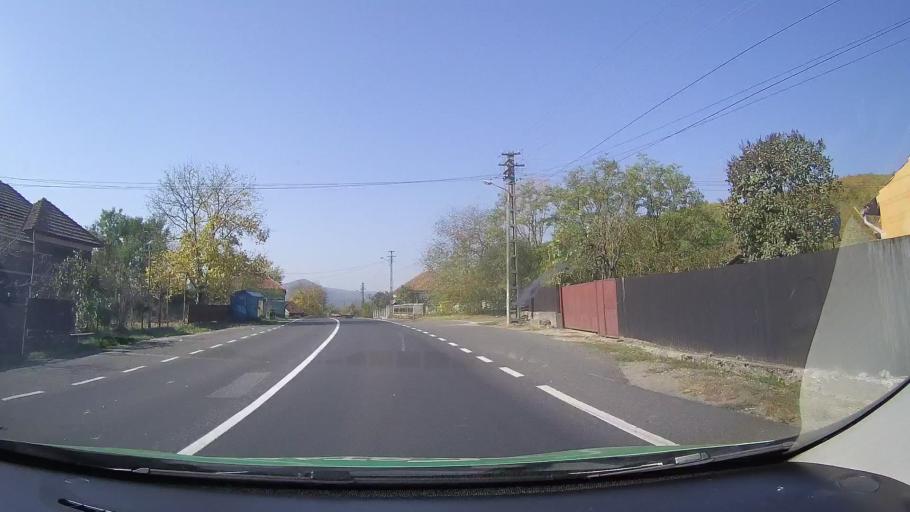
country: RO
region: Hunedoara
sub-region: Comuna Dobra
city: Dobra
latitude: 45.9396
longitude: 22.5390
